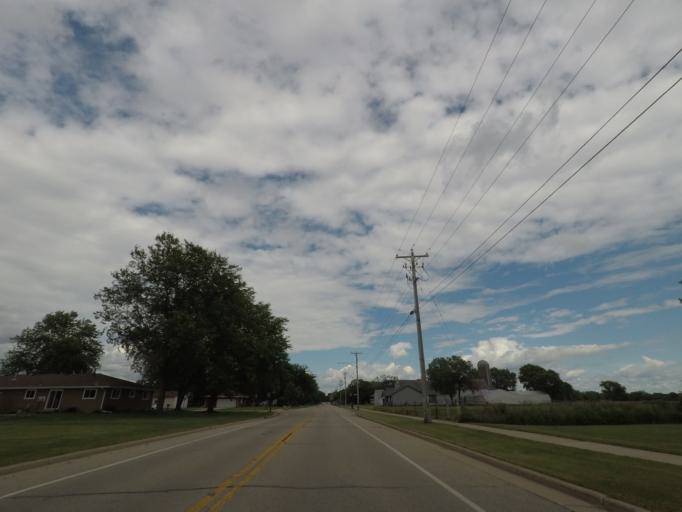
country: US
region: Wisconsin
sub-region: Green County
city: Brooklyn
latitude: 42.8536
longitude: -89.3793
